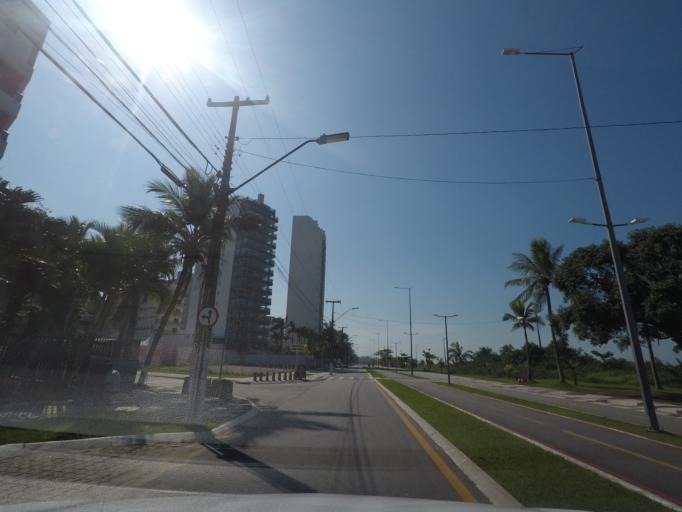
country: BR
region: Parana
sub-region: Guaratuba
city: Guaratuba
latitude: -25.8421
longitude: -48.5392
